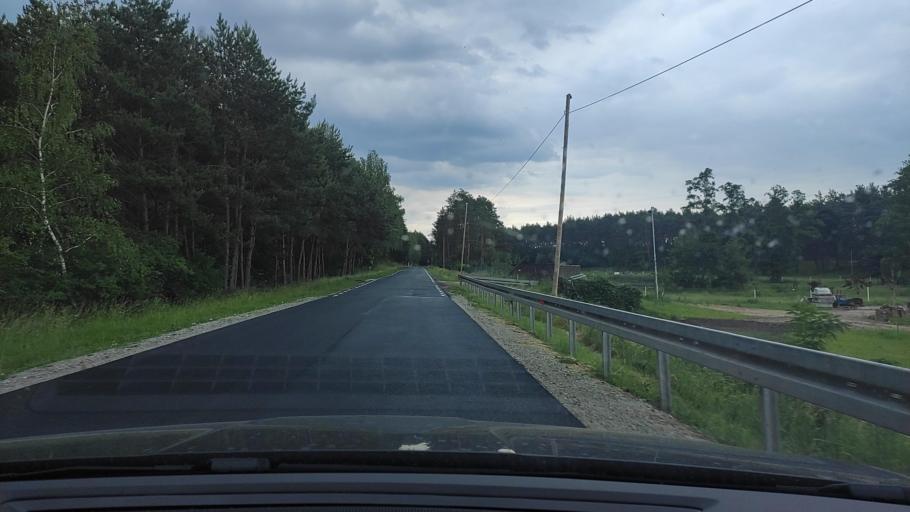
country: PL
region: Greater Poland Voivodeship
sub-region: Powiat poznanski
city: Pobiedziska
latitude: 52.5026
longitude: 17.2244
